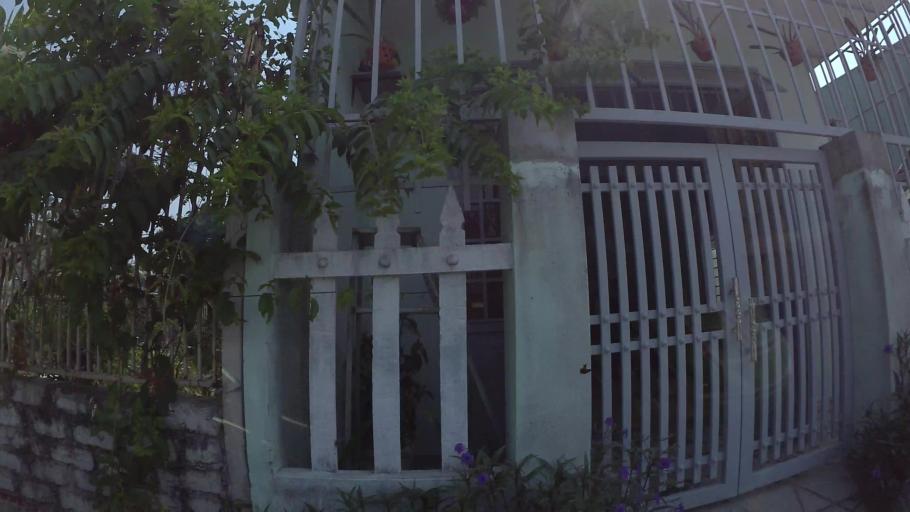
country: VN
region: Da Nang
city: Ngu Hanh Son
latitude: 15.9909
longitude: 108.2414
